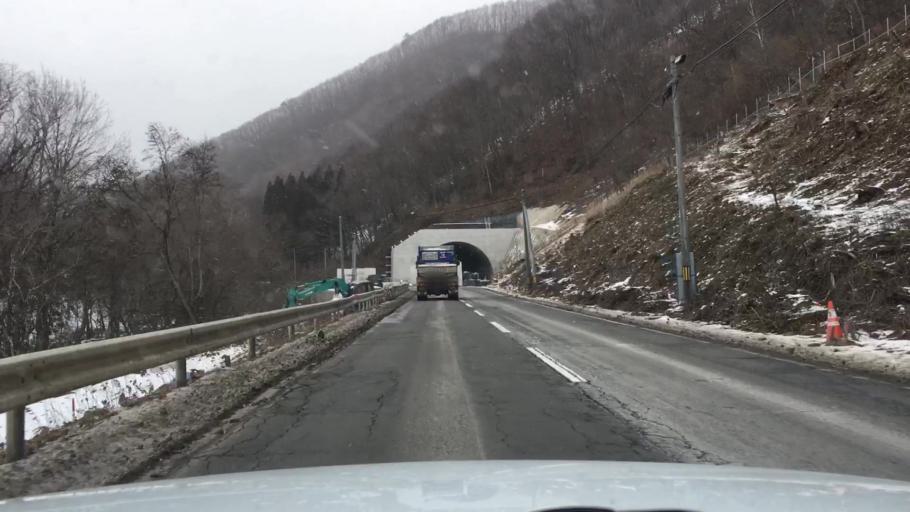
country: JP
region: Iwate
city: Tono
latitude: 39.6252
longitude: 141.4697
